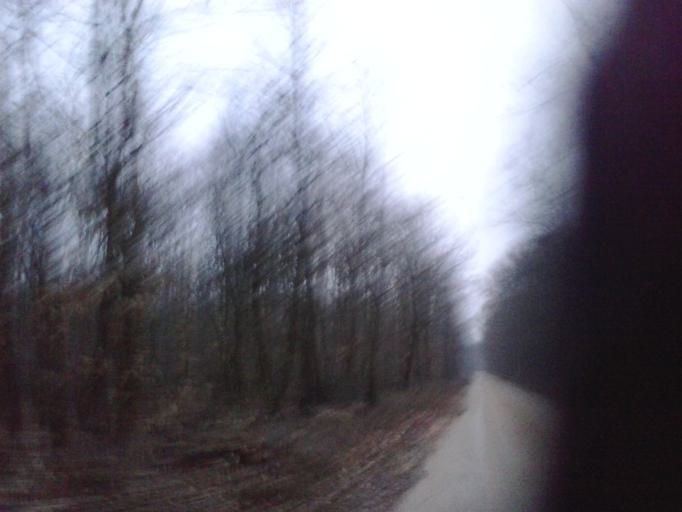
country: HU
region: Vas
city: Sarvar
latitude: 47.1379
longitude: 16.9839
